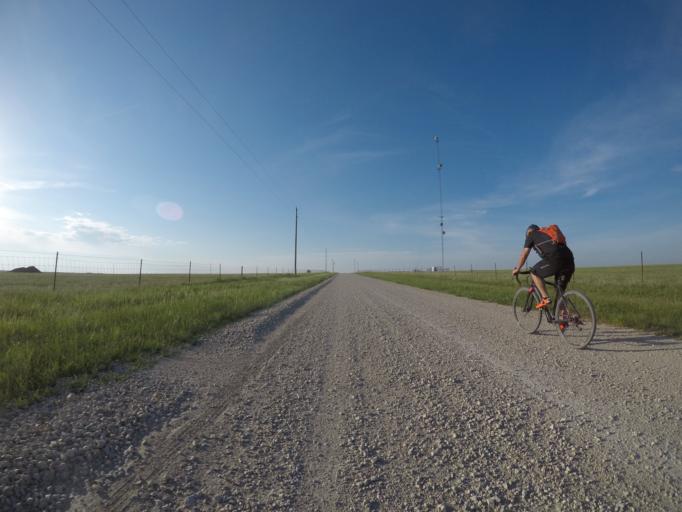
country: US
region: Kansas
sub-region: Riley County
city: Manhattan
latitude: 39.0271
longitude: -96.4918
